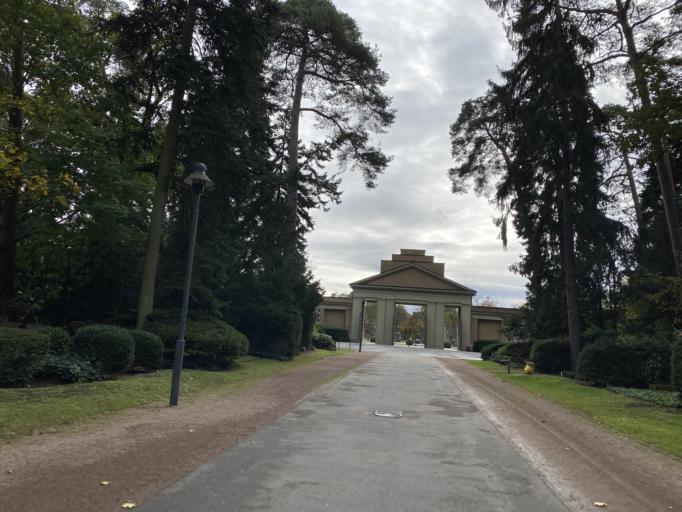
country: DE
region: Hesse
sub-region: Regierungsbezirk Darmstadt
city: Darmstadt
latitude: 49.8712
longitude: 8.6126
